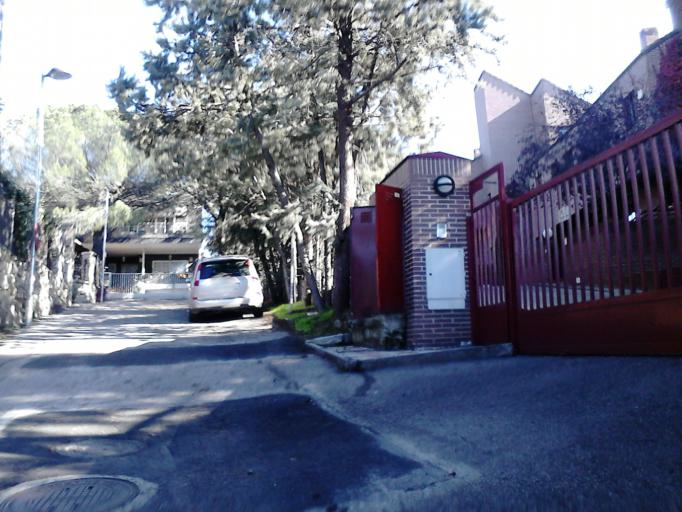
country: ES
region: Madrid
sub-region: Provincia de Madrid
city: Torrelodones
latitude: 40.5867
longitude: -3.9648
